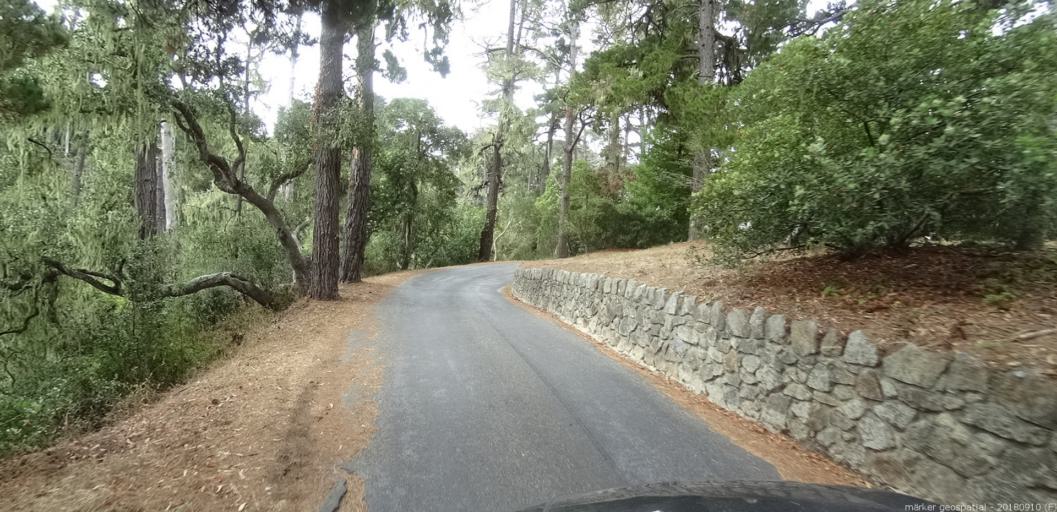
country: US
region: California
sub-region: Monterey County
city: Carmel-by-the-Sea
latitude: 36.5039
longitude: -121.9323
